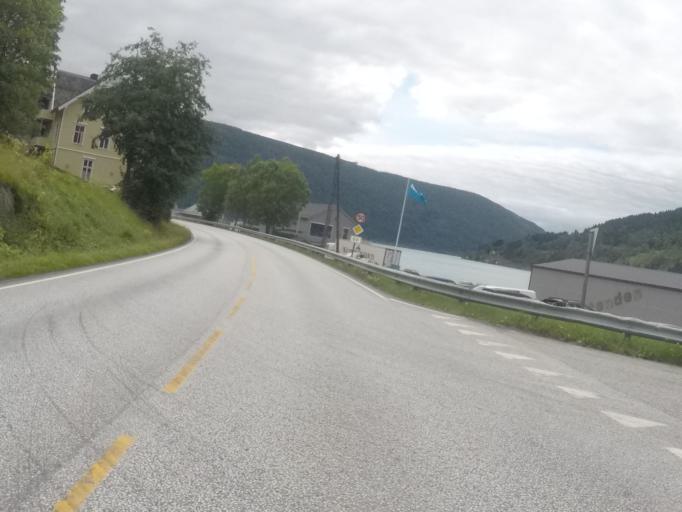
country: NO
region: Sogn og Fjordane
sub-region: Stryn
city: Stryn
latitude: 61.8977
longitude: 6.7070
